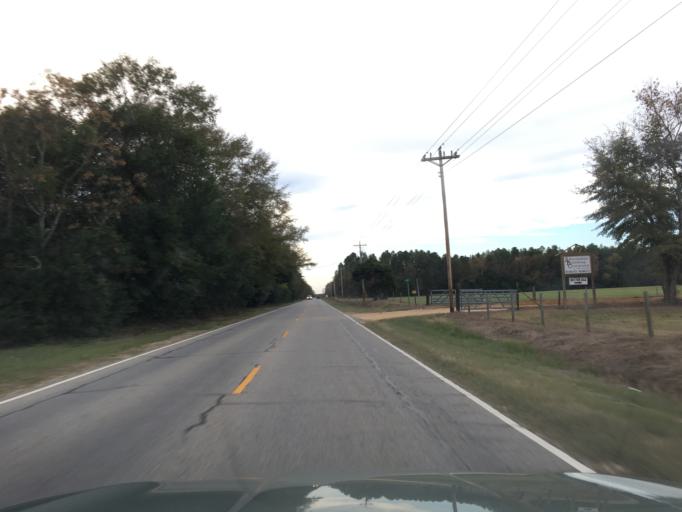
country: US
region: South Carolina
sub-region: Lexington County
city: Leesville
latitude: 33.7773
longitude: -81.3993
